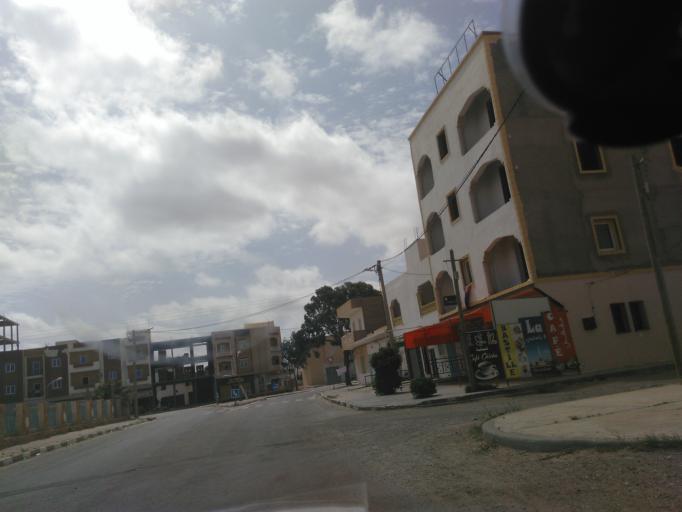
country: TN
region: Tataouine
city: Tataouine
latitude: 32.9547
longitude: 10.4681
